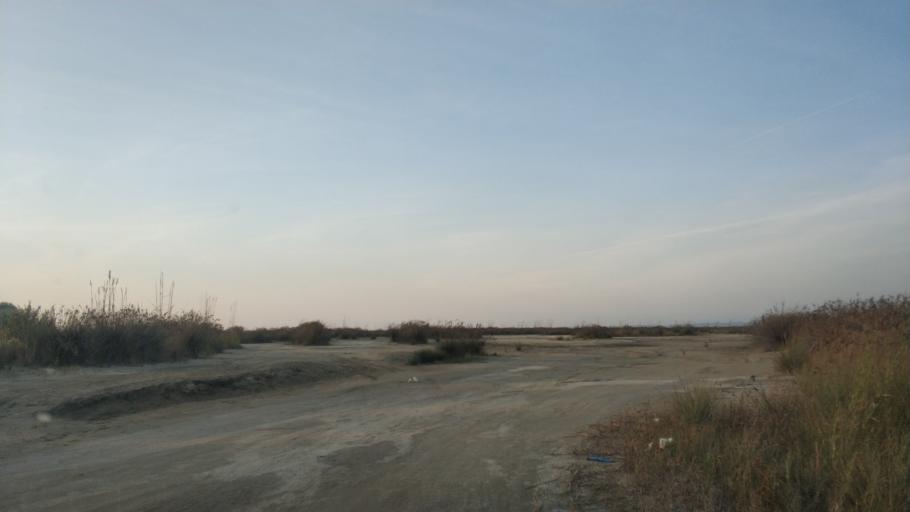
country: AL
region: Fier
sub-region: Rrethi i Lushnjes
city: Divjake
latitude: 40.9554
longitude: 19.4711
